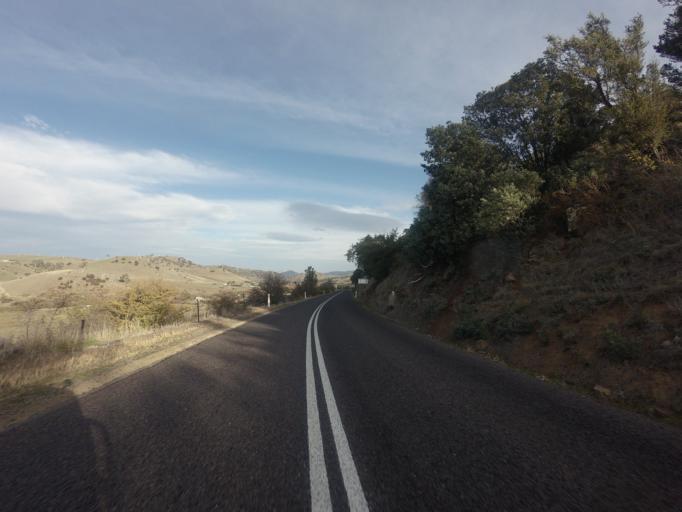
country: AU
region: Tasmania
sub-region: Brighton
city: Bridgewater
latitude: -42.4202
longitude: 147.1406
